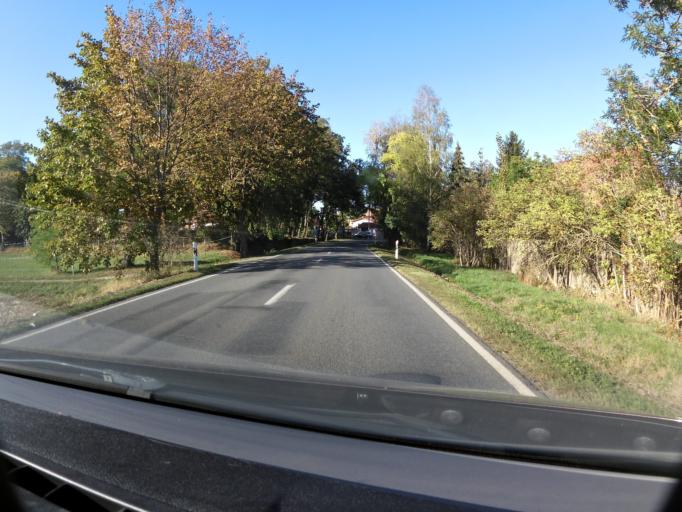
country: DE
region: Saxony-Anhalt
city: Groeningen
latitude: 51.9174
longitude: 11.1917
